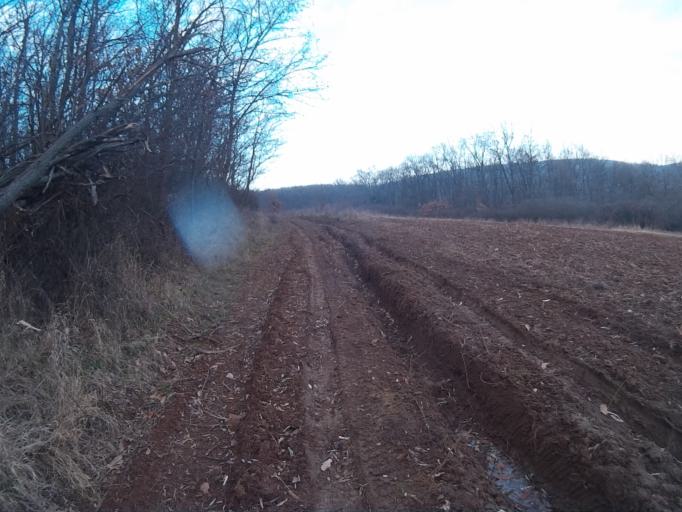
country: HU
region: Nograd
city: Rimoc
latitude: 47.9948
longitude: 19.4306
